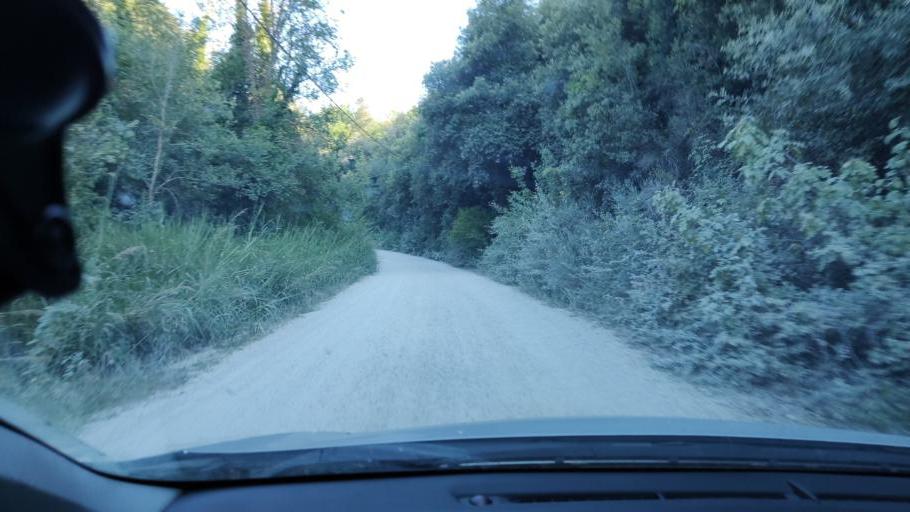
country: IT
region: Umbria
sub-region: Provincia di Terni
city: Amelia
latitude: 42.5411
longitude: 12.3816
